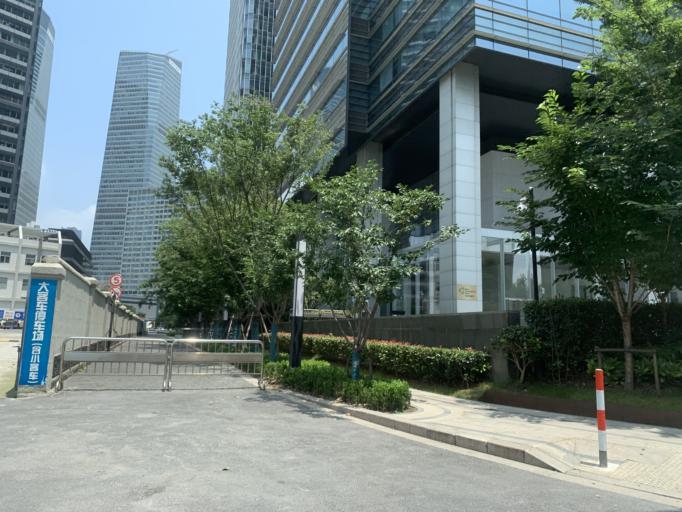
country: CN
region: Shanghai Shi
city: Hongkou
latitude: 31.2346
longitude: 121.4987
